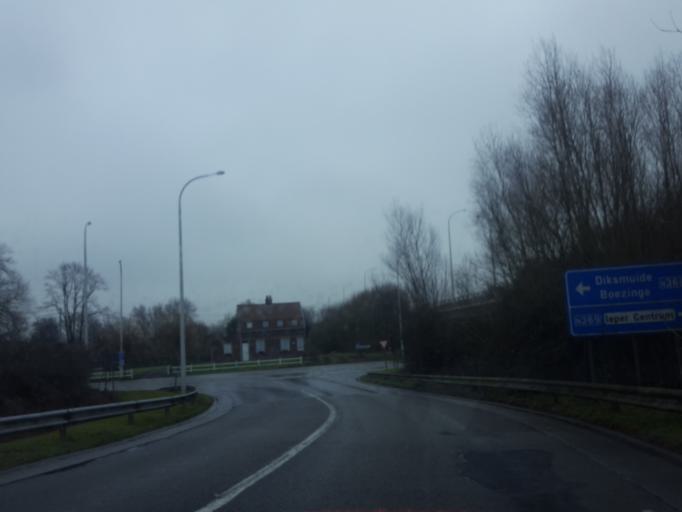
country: BE
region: Flanders
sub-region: Provincie West-Vlaanderen
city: Ieper
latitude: 50.8699
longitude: 2.8722
